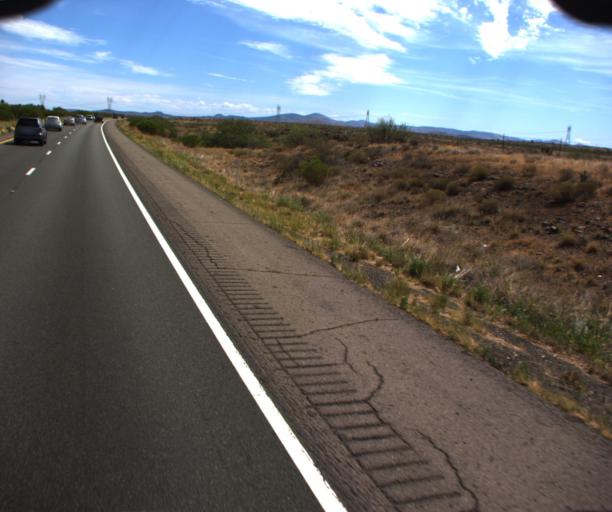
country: US
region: Arizona
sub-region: Yavapai County
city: Spring Valley
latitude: 34.3728
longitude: -112.1086
